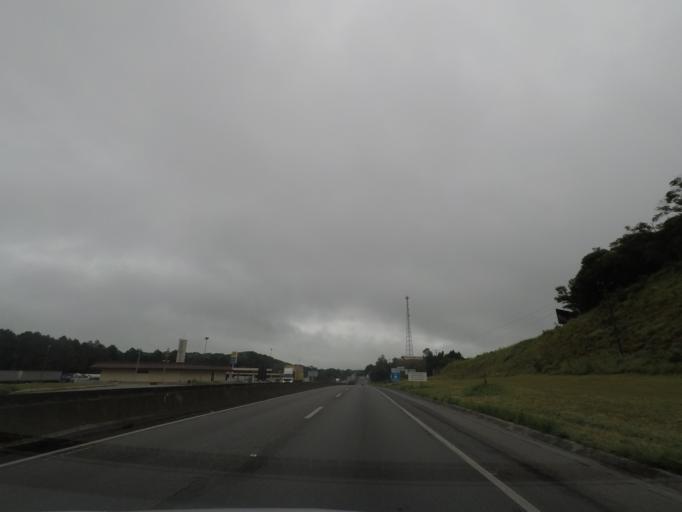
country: BR
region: Parana
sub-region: Campina Grande Do Sul
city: Campina Grande do Sul
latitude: -25.3296
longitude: -49.0300
